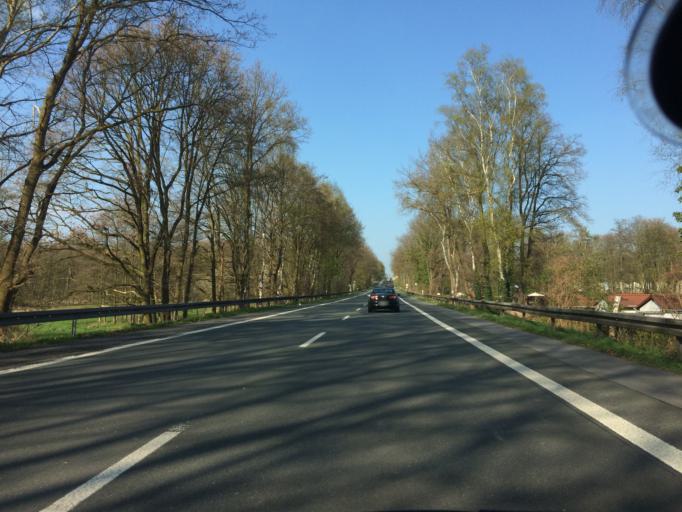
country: DE
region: North Rhine-Westphalia
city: Herten
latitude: 51.5621
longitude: 7.1210
